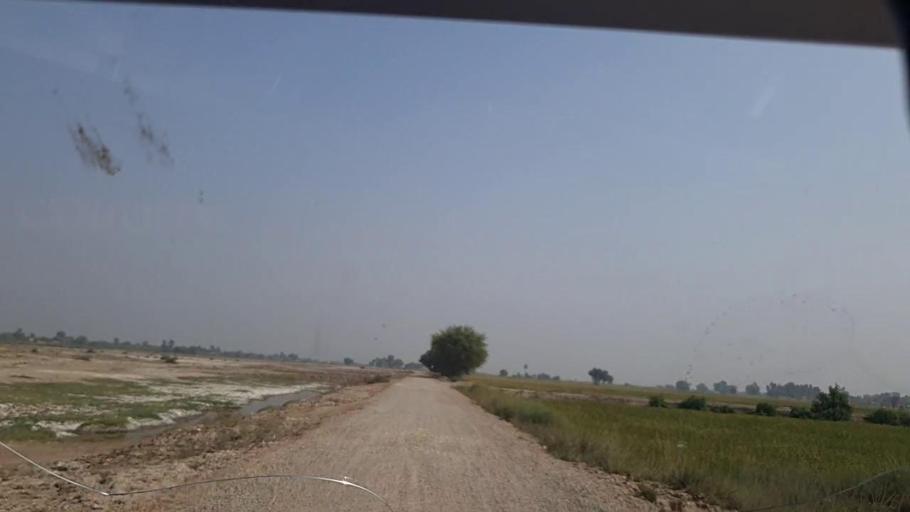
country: PK
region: Sindh
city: Shikarpur
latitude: 28.0513
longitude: 68.6651
